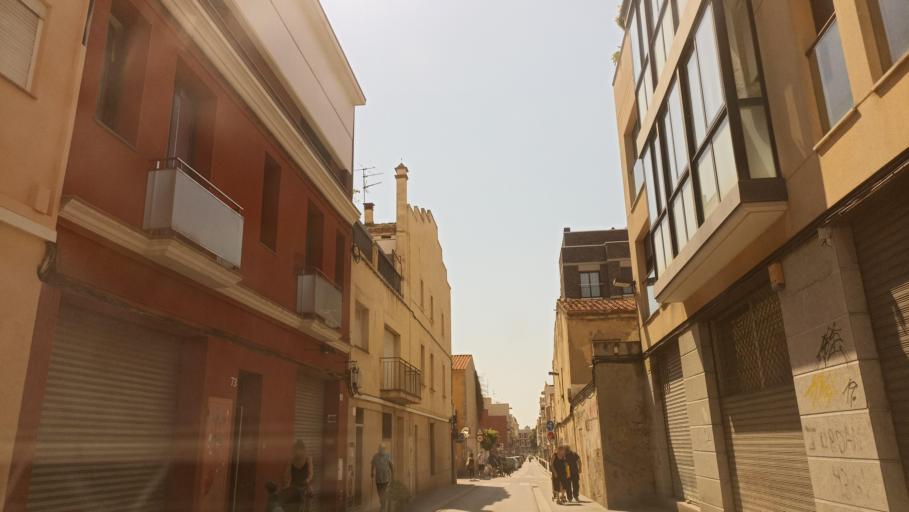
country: ES
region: Catalonia
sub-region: Provincia de Barcelona
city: Mataro
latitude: 41.5360
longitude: 2.4421
